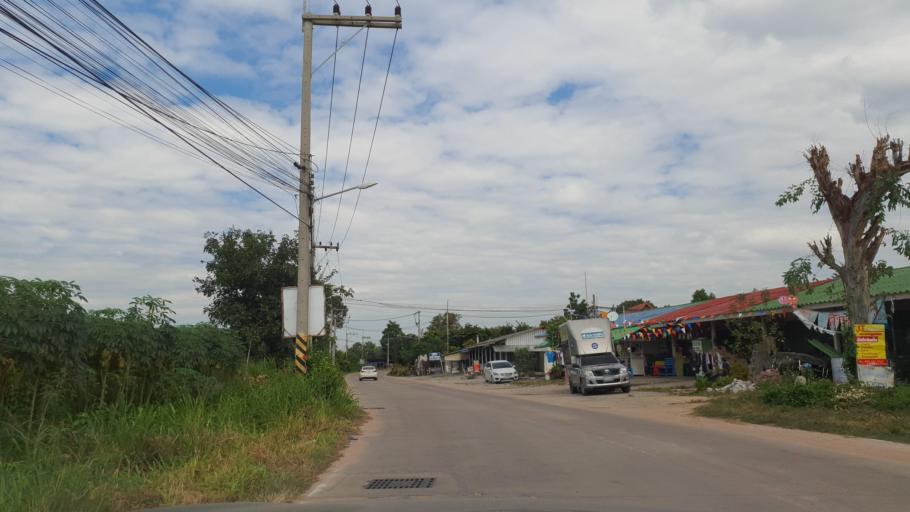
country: TH
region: Chon Buri
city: Phatthaya
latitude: 12.9472
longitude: 100.9483
